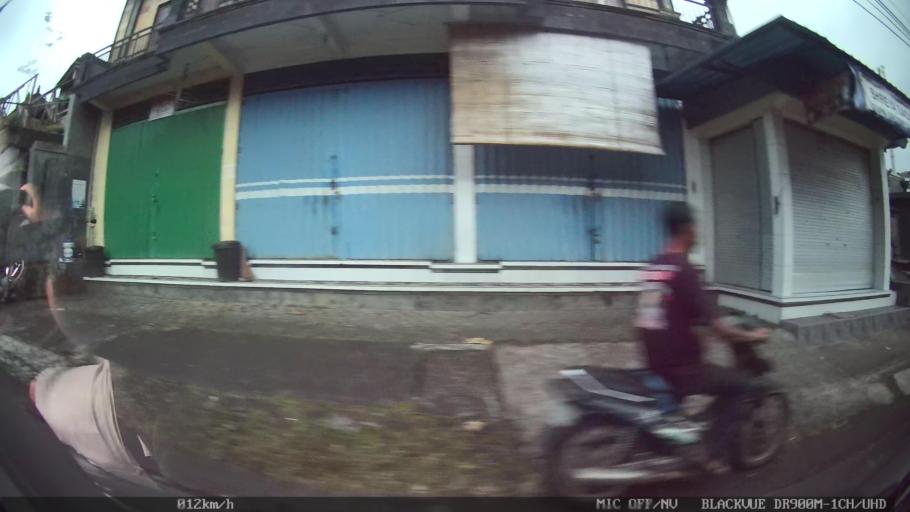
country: ID
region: Bali
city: Banjar Triwangsakeliki
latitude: -8.4491
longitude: 115.2625
